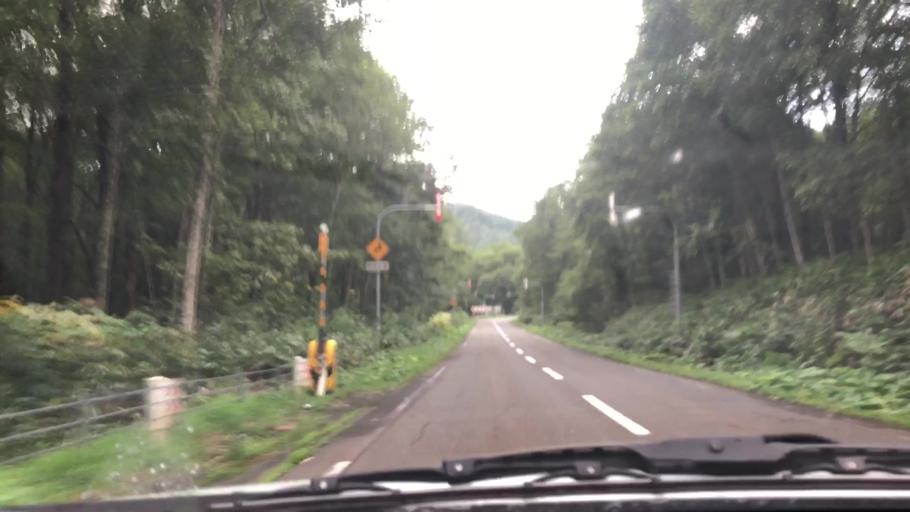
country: JP
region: Hokkaido
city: Shimo-furano
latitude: 42.9223
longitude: 142.3747
